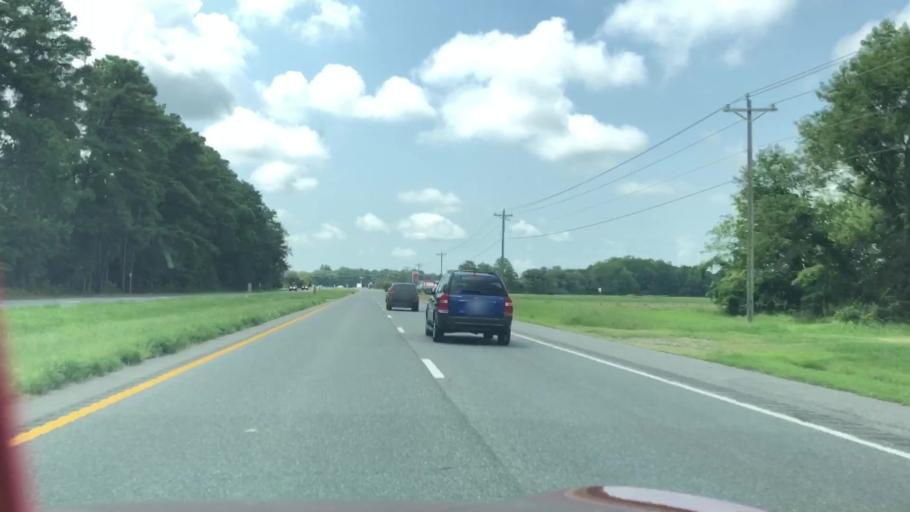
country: US
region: Virginia
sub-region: Northampton County
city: Eastville
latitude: 37.3075
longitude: -75.9642
